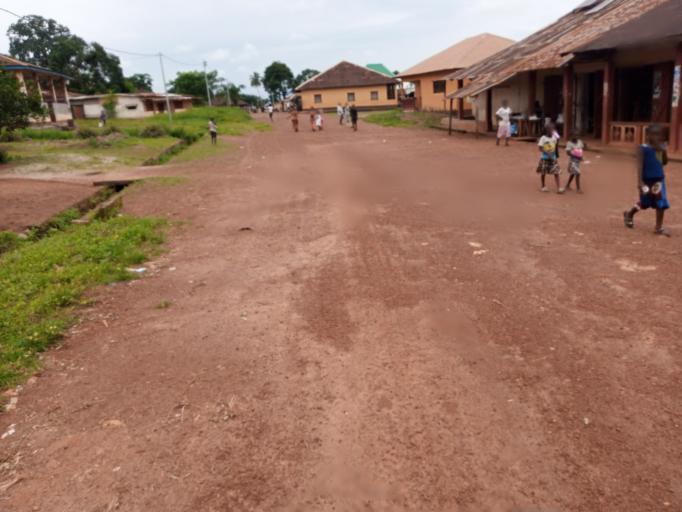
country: SL
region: Southern Province
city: Largo
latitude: 8.2040
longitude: -12.0609
